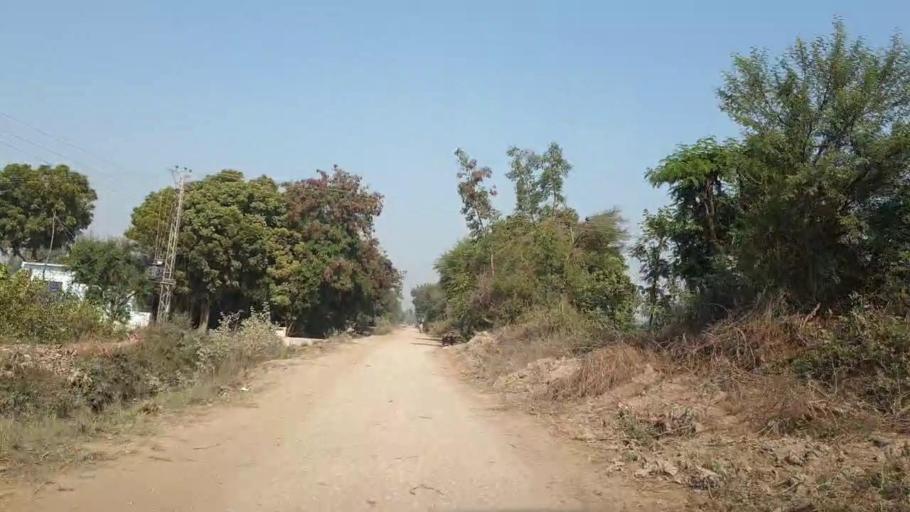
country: PK
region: Sindh
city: Tando Allahyar
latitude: 25.4658
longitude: 68.6932
